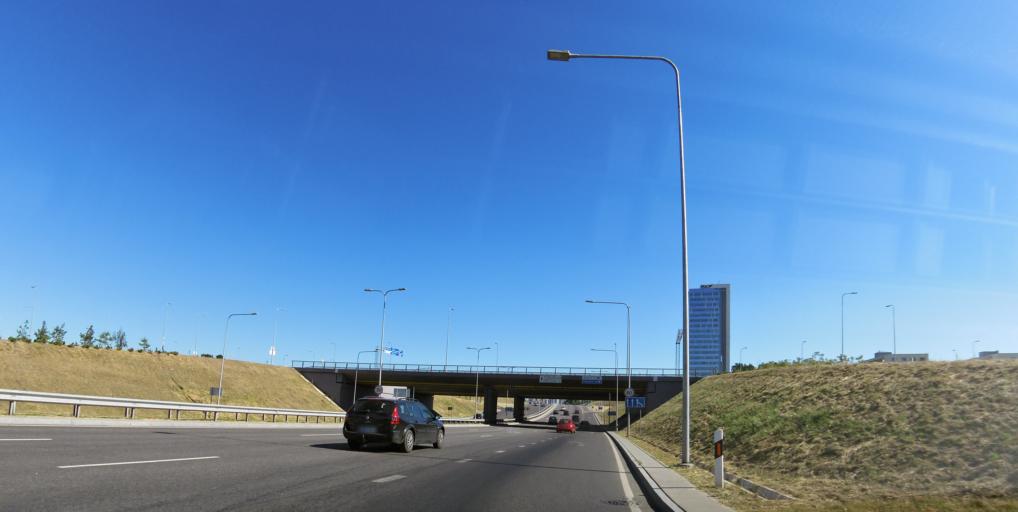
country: LT
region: Vilnius County
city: Justiniskes
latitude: 54.6995
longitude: 25.2081
